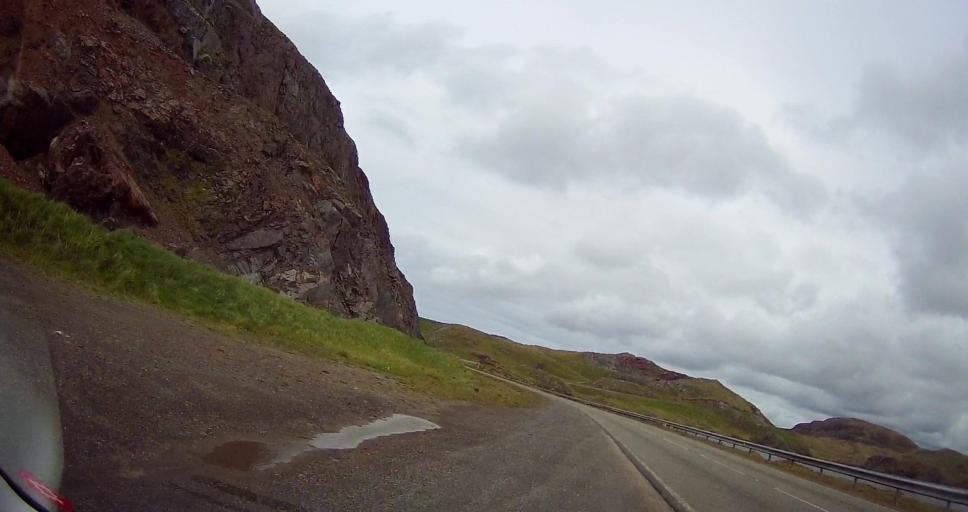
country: GB
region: Scotland
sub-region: Shetland Islands
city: Lerwick
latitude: 60.3954
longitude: -1.3792
